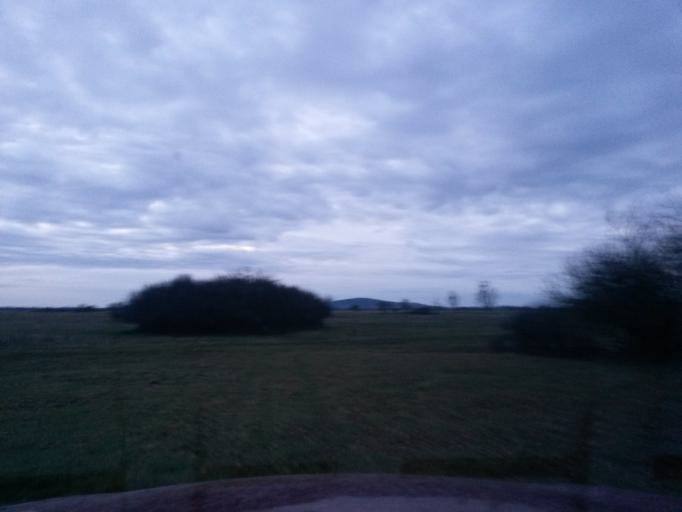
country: HU
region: Borsod-Abauj-Zemplen
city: Karcsa
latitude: 48.4175
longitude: 21.8746
